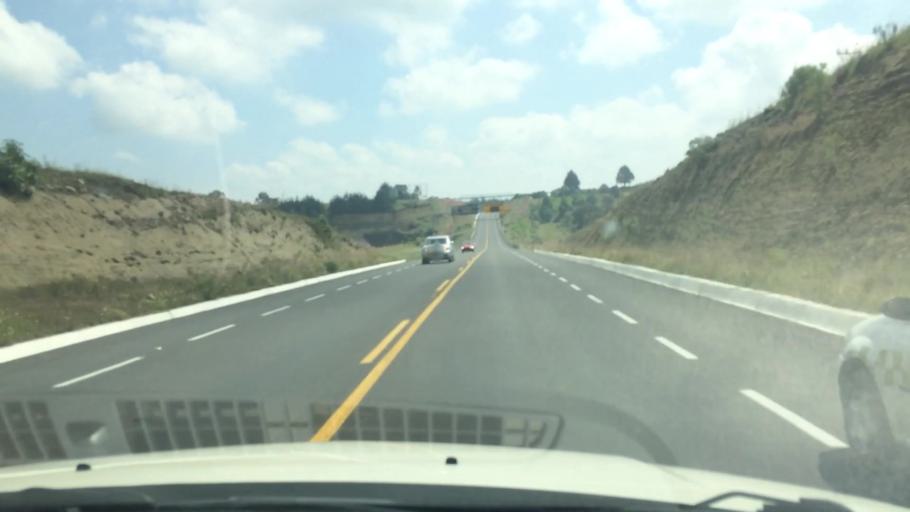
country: MX
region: Mexico
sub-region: Villa Victoria
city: Colonia Doctor Gustavo Baz
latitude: 19.3765
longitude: -99.8885
